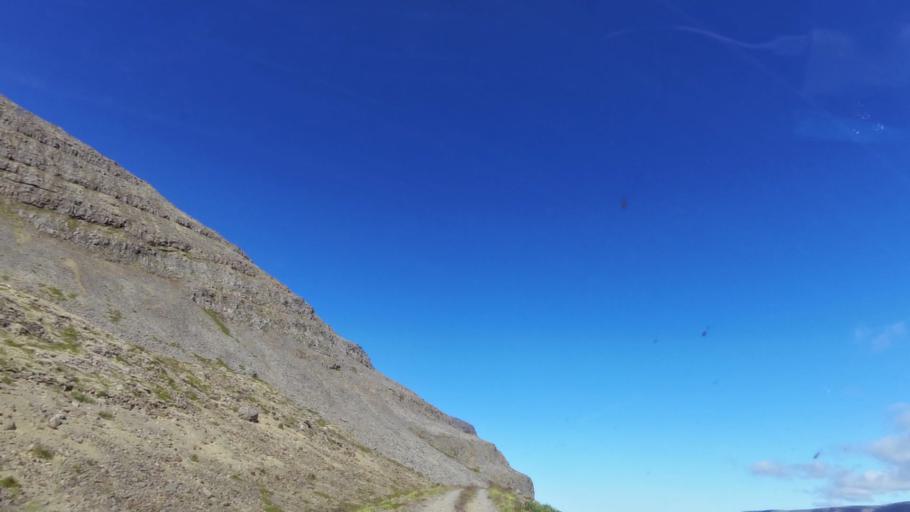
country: IS
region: West
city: Olafsvik
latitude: 65.6225
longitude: -23.8820
